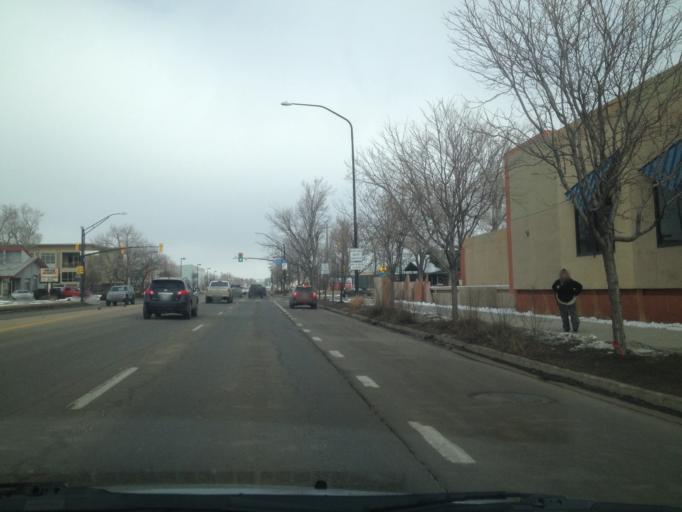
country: US
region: Colorado
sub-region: Boulder County
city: Boulder
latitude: 40.0248
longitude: -105.2583
